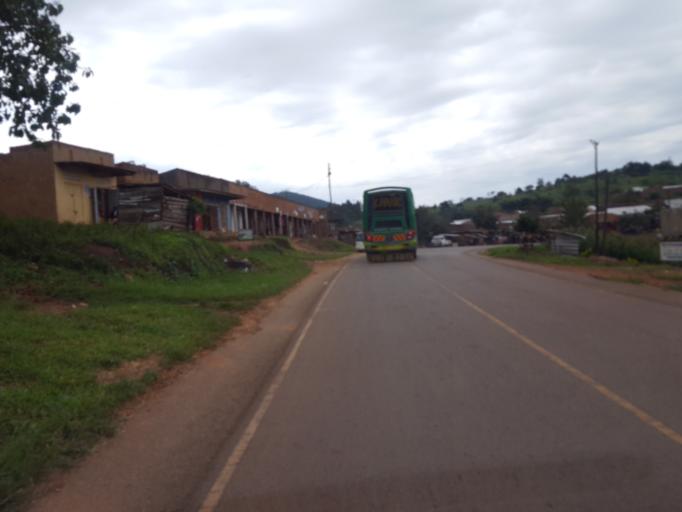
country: UG
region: Central Region
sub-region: Mityana District
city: Mityana
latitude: 0.6726
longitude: 32.0853
